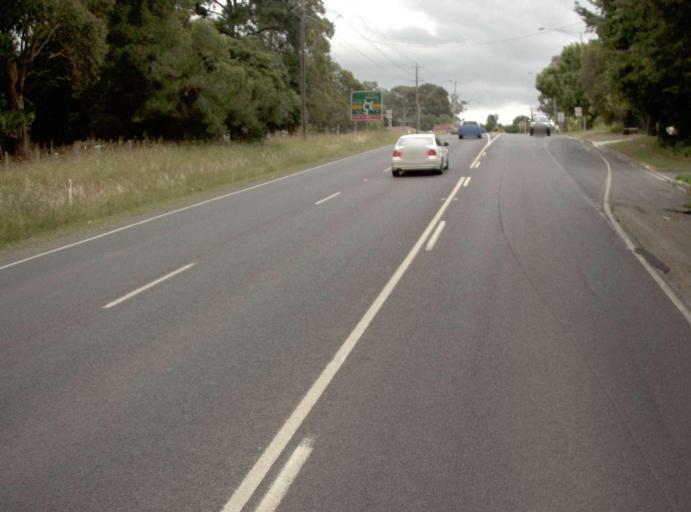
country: AU
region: Victoria
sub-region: Yarra Ranges
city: Mount Evelyn
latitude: -37.7809
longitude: 145.4348
